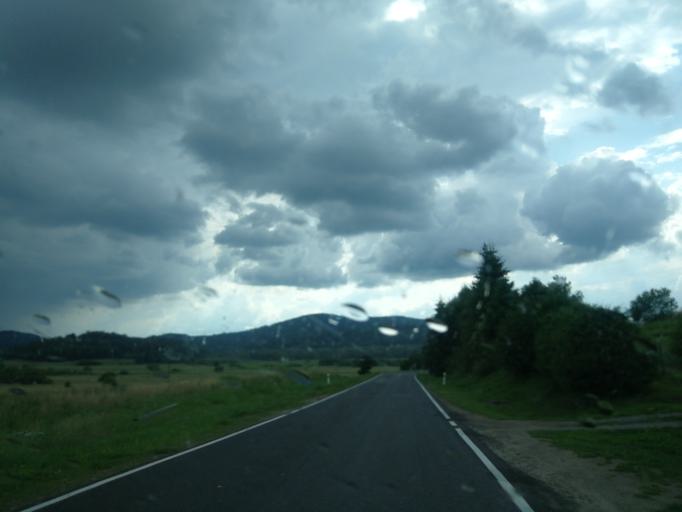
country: PL
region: Subcarpathian Voivodeship
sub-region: Powiat leski
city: Uherce Mineralne
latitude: 49.4578
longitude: 22.4129
